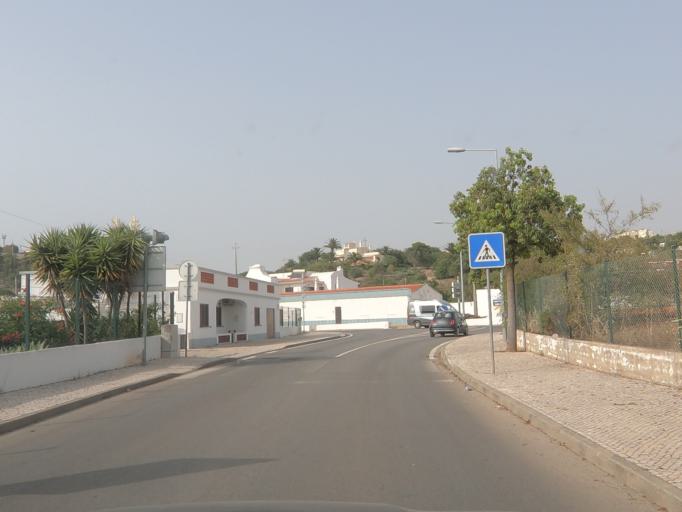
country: PT
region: Faro
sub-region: Albufeira
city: Guia
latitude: 37.0880
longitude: -8.2938
